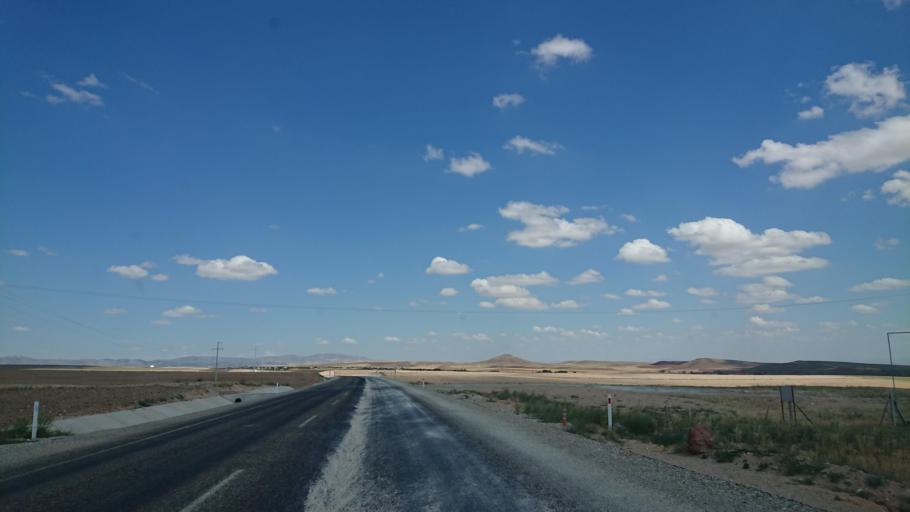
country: TR
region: Kirsehir
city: Kirsehir
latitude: 39.1221
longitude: 34.0077
